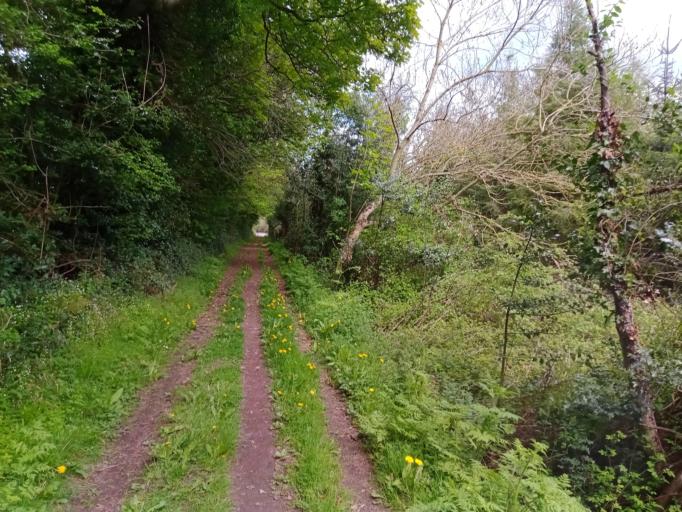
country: IE
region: Leinster
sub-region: Kilkenny
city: Ballyragget
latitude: 52.7236
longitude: -7.4141
